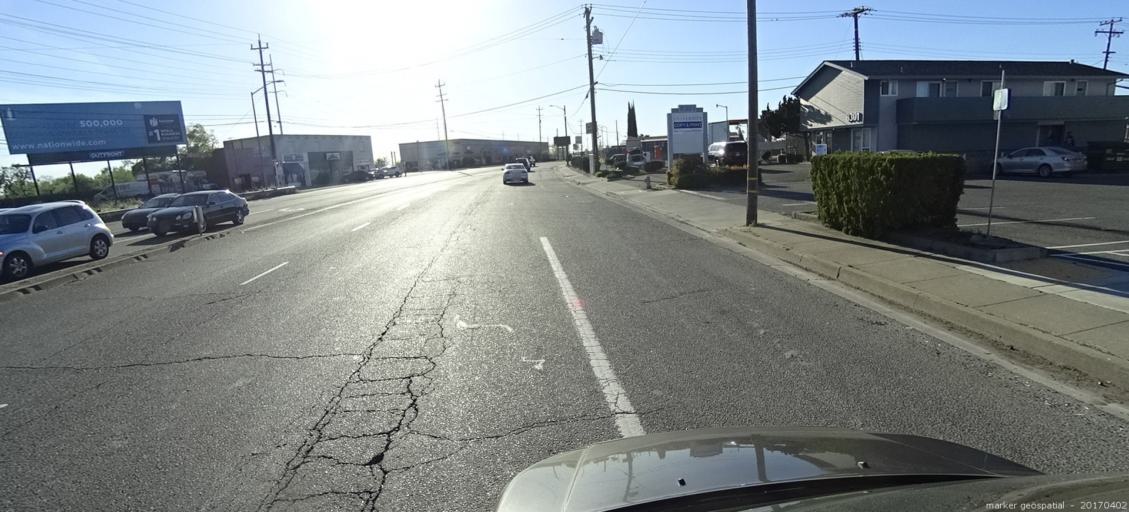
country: US
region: California
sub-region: Sacramento County
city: Rosemont
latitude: 38.5471
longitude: -121.3992
